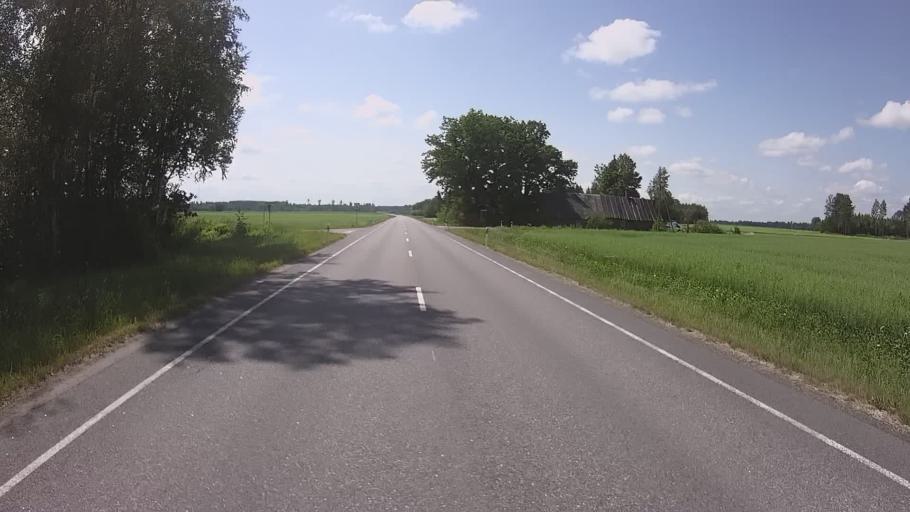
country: EE
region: Tartu
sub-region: Tartu linn
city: Tartu
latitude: 58.3943
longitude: 26.8936
